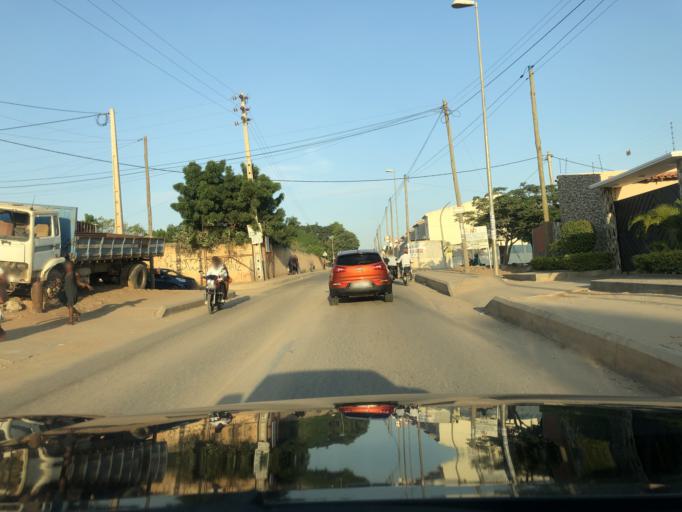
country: AO
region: Luanda
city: Luanda
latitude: -8.9451
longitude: 13.1600
